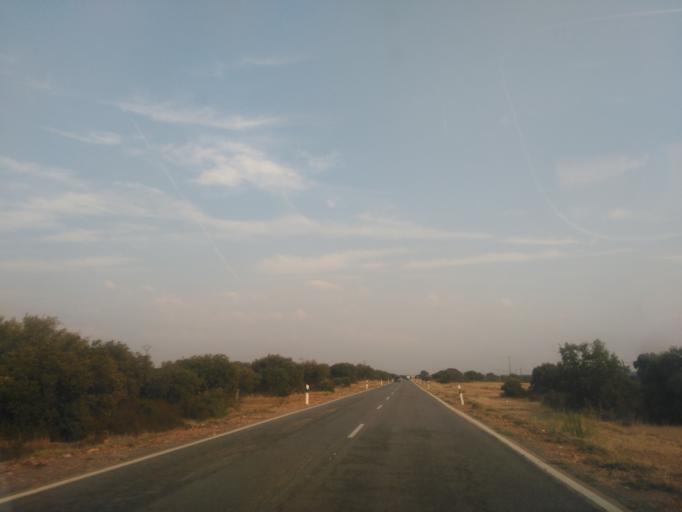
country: ES
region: Castille and Leon
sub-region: Provincia de Zamora
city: Perilla de Castro
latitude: 41.7275
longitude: -5.8185
